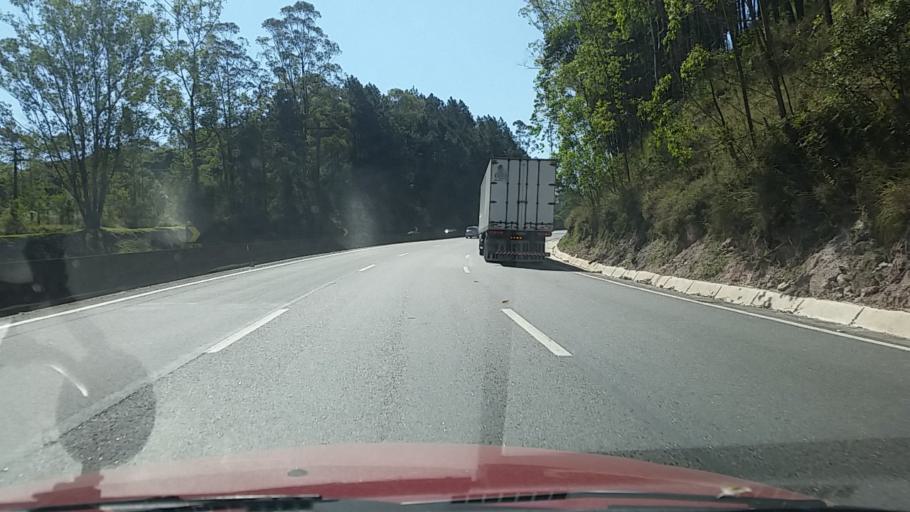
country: BR
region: Sao Paulo
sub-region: Sao Lourenco Da Serra
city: Sao Lourenco da Serra
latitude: -23.7952
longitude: -46.9151
